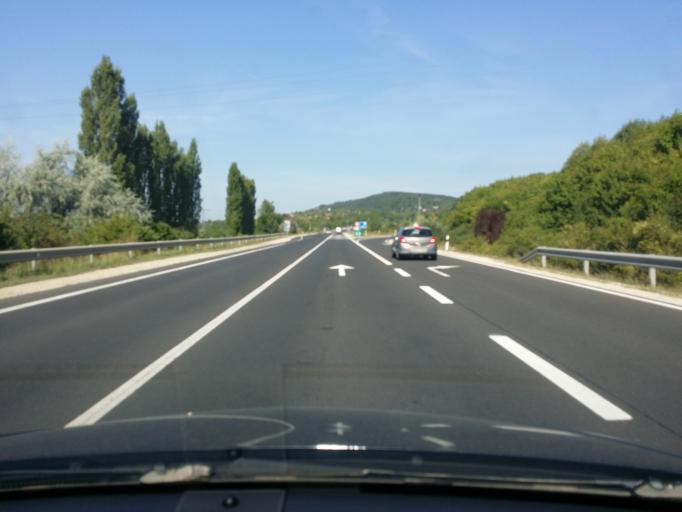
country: HU
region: Pest
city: Vac
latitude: 47.8152
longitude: 19.1019
